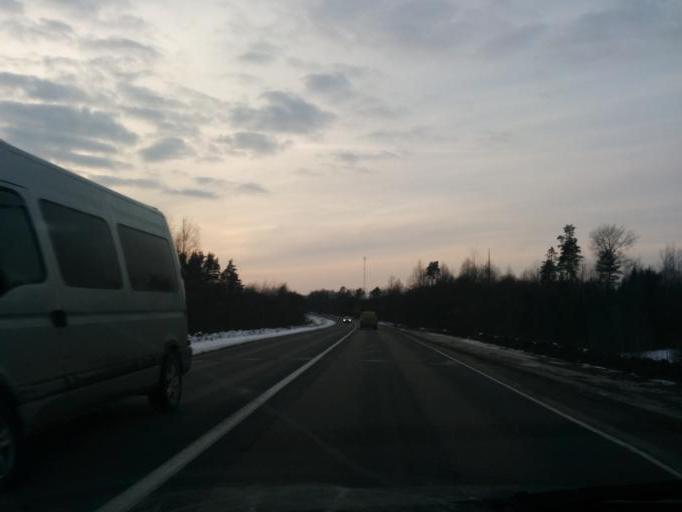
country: LV
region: Raunas
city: Rauna
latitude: 57.3197
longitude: 25.7025
